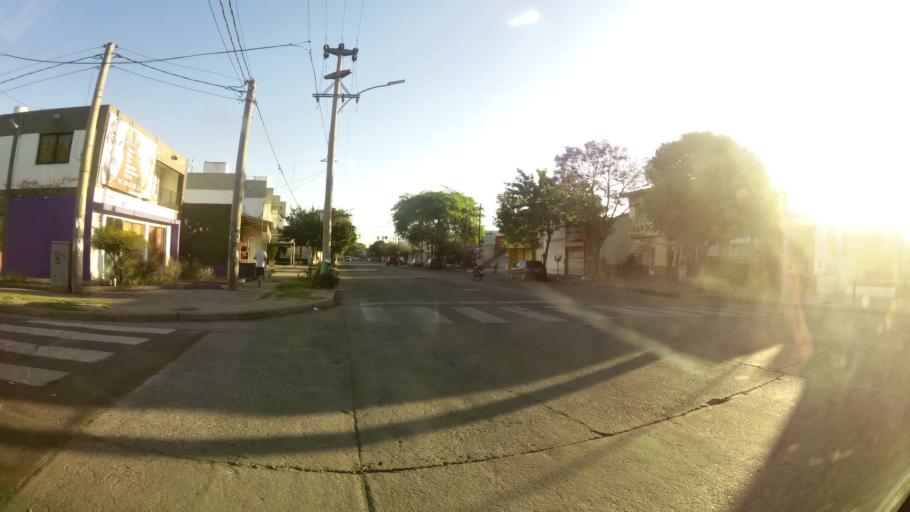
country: AR
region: Cordoba
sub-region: Departamento de Capital
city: Cordoba
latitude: -31.3731
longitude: -64.2061
